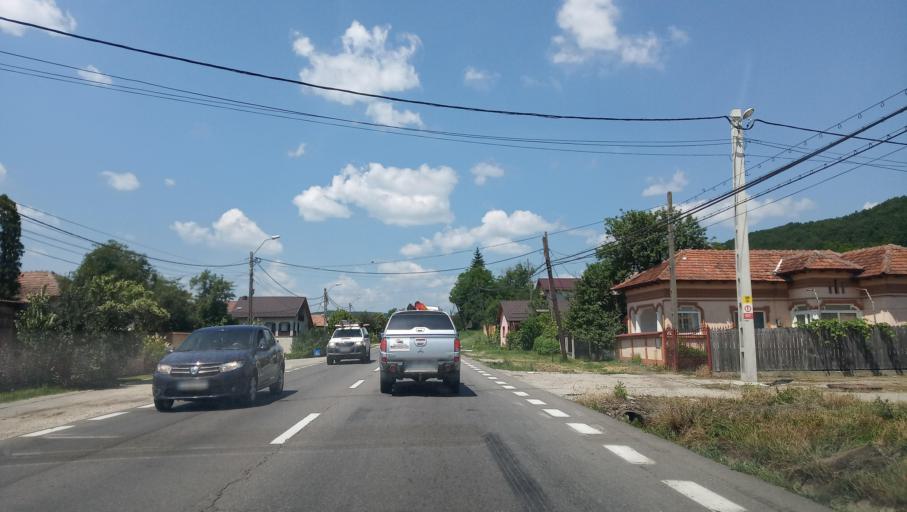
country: RO
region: Arges
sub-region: Comuna Bascov
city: Bascov
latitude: 44.8893
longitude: 24.7667
